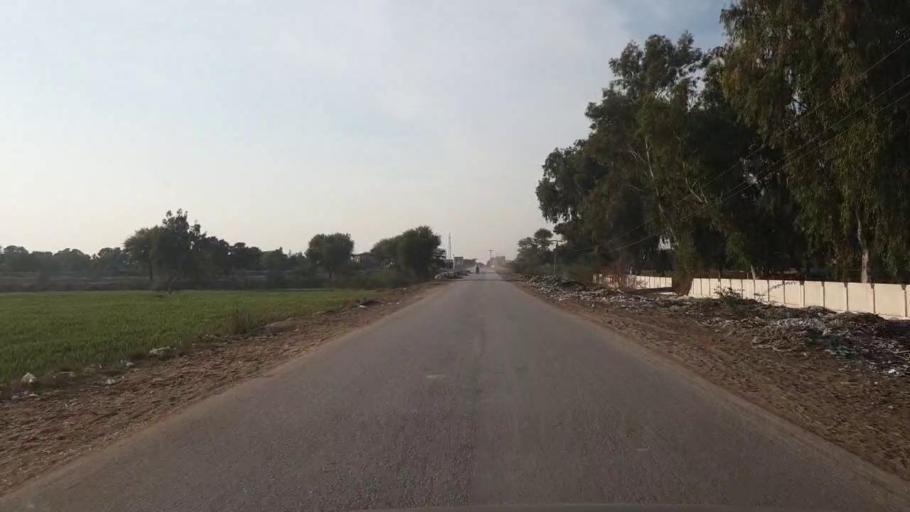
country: PK
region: Sindh
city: Shahpur Chakar
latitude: 26.1571
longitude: 68.6426
